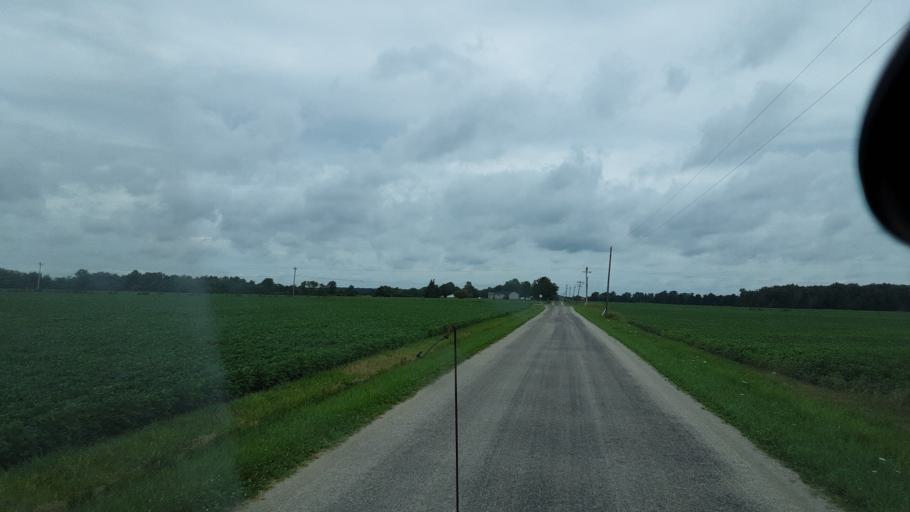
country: US
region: Indiana
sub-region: Jay County
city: Portland
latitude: 40.5094
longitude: -85.0096
